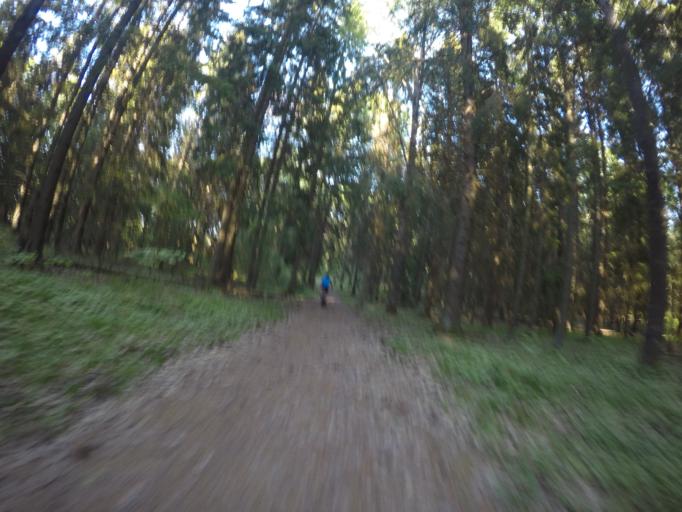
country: SE
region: Soedermanland
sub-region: Eskilstuna Kommun
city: Eskilstuna
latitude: 59.3517
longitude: 16.5201
